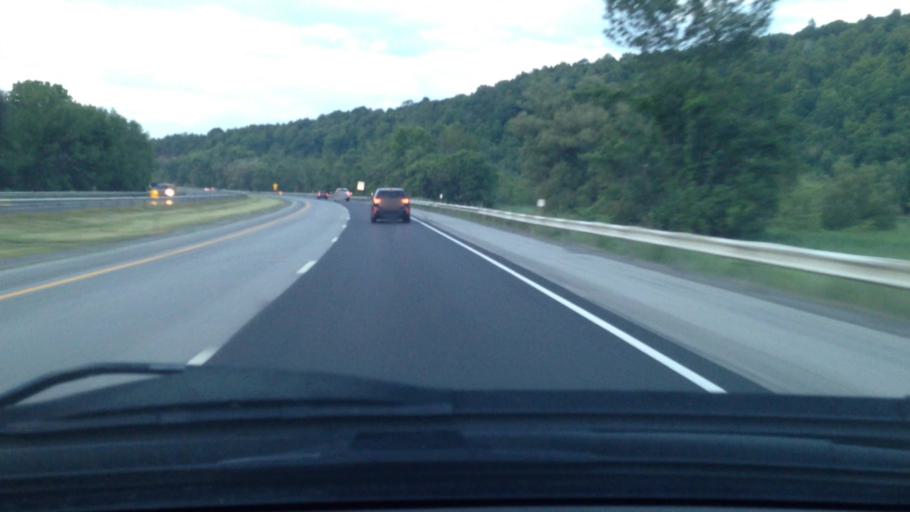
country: US
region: New York
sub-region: Montgomery County
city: Fonda
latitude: 42.8980
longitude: -74.4644
